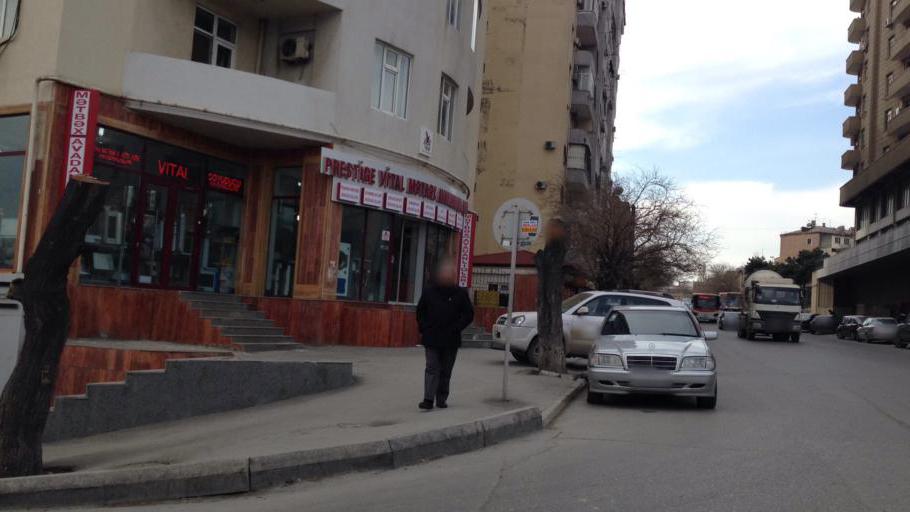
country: AZ
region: Baki
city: Baku
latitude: 40.3857
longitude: 49.8512
